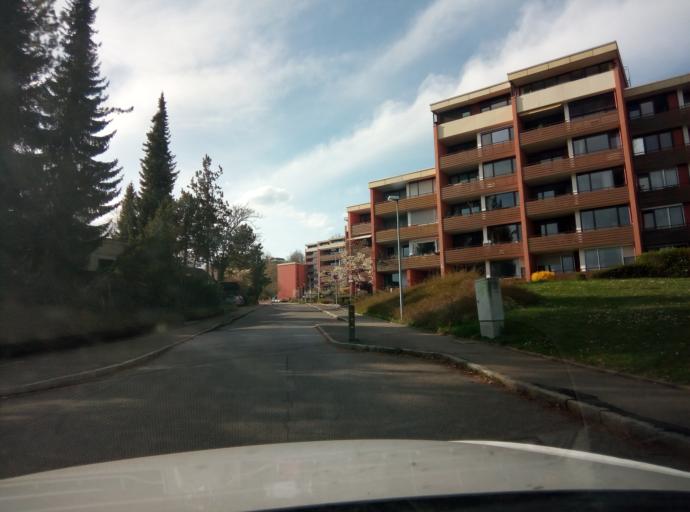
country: DE
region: Baden-Wuerttemberg
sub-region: Tuebingen Region
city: Tuebingen
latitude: 48.5398
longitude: 9.0687
